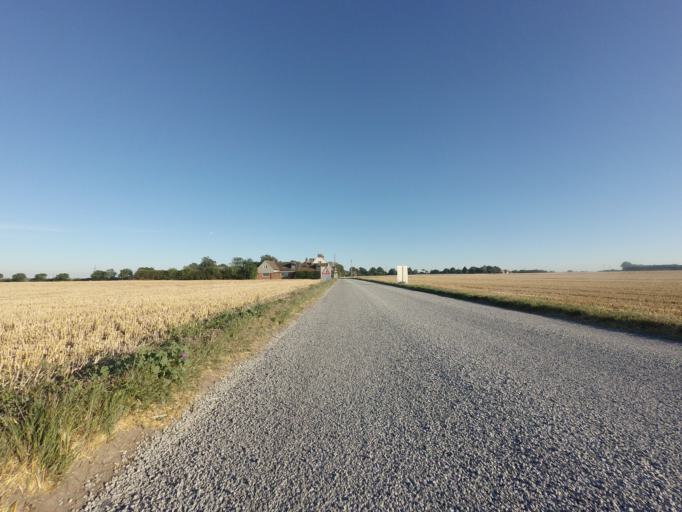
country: GB
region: England
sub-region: Kent
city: Herne Bay
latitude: 51.3377
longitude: 1.1902
